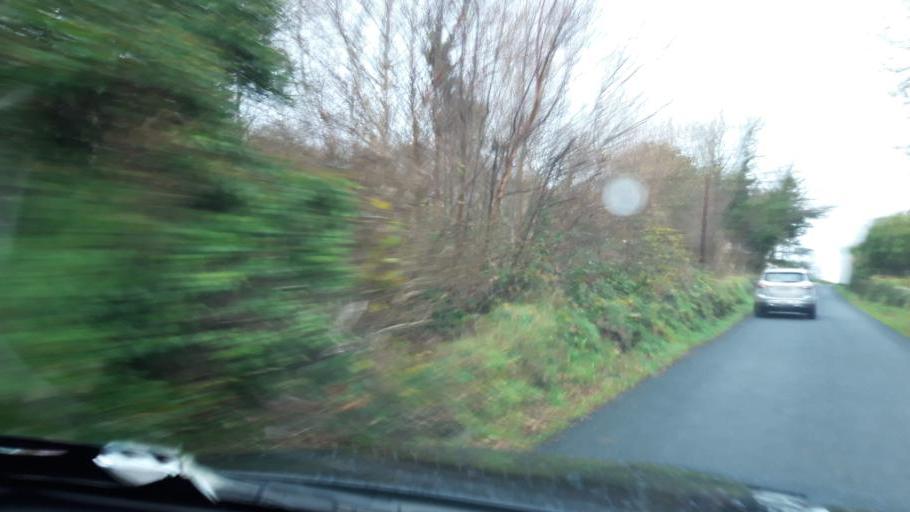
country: IE
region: Ulster
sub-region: County Donegal
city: Buncrana
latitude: 55.2348
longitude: -7.6181
